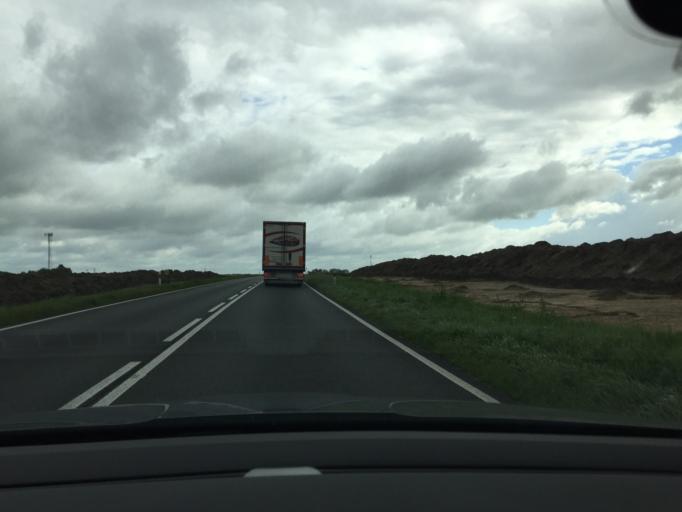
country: PL
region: West Pomeranian Voivodeship
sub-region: Powiat gryficki
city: Ploty
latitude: 53.7399
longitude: 15.2100
